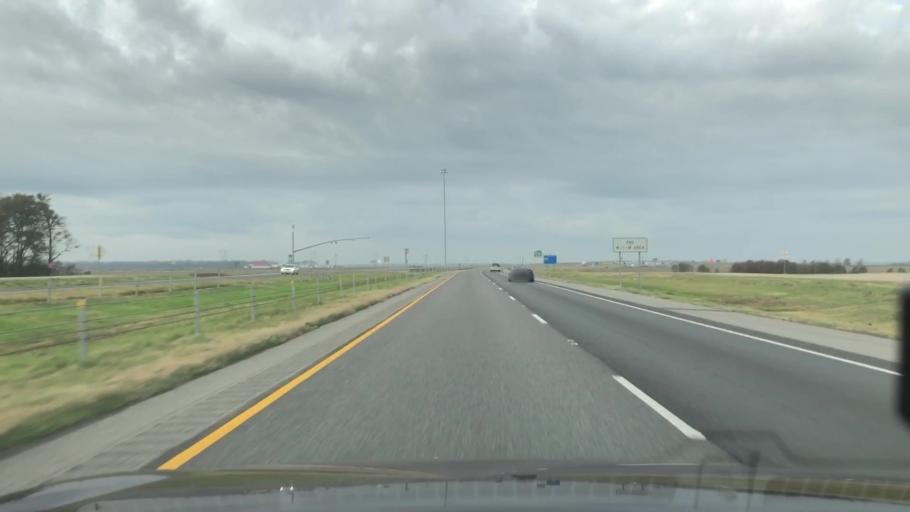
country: US
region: Mississippi
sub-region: Warren County
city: Vicksburg
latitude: 32.3201
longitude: -90.9478
